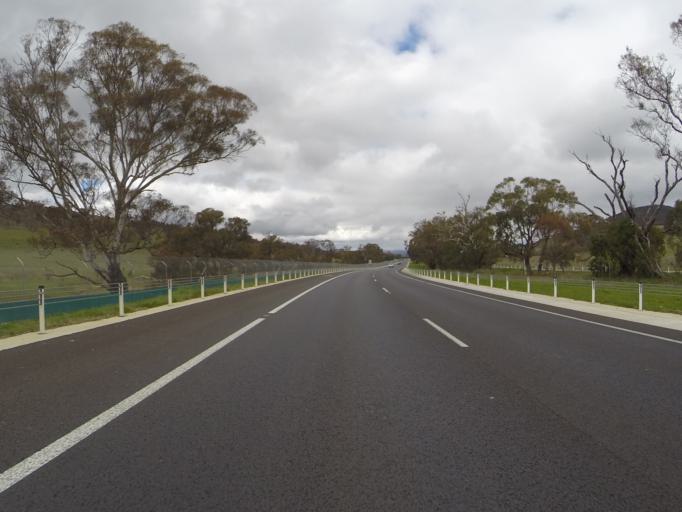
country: AU
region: Australian Capital Territory
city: Kaleen
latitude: -35.2191
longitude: 149.1959
